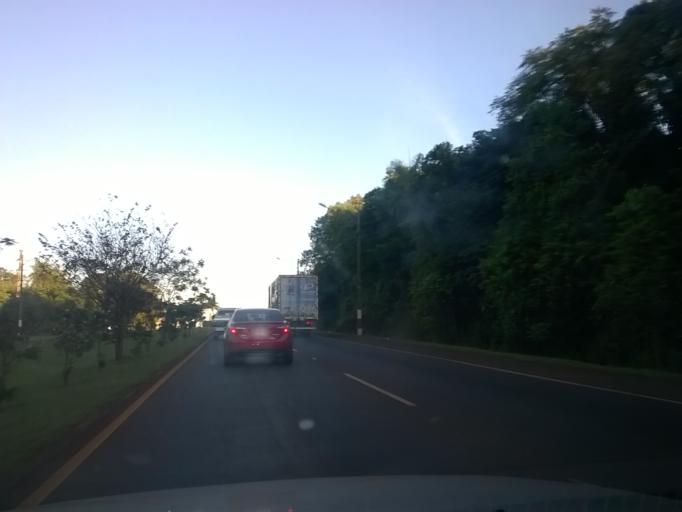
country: PY
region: Alto Parana
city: Ciudad del Este
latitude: -25.4466
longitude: -54.6302
